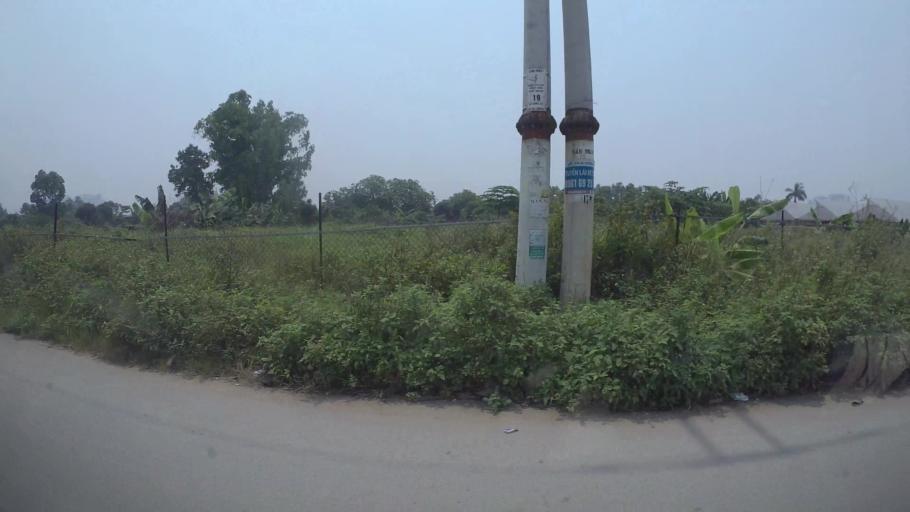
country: VN
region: Ha Noi
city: Ha Dong
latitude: 20.9975
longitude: 105.7677
